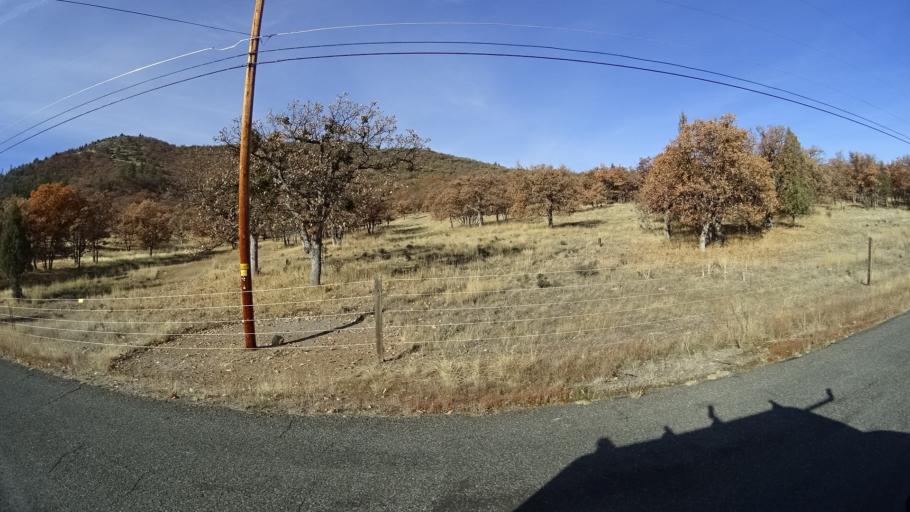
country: US
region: California
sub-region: Siskiyou County
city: Yreka
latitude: 41.6596
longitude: -122.6251
